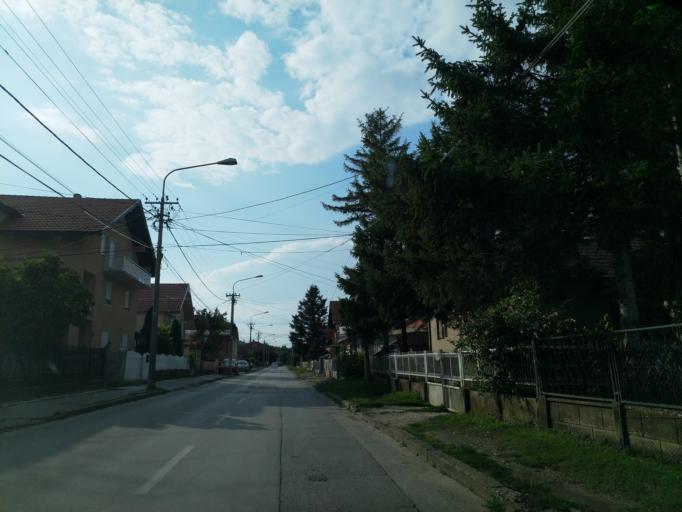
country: RS
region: Central Serbia
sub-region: Pomoravski Okrug
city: Jagodina
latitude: 43.9747
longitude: 21.2522
